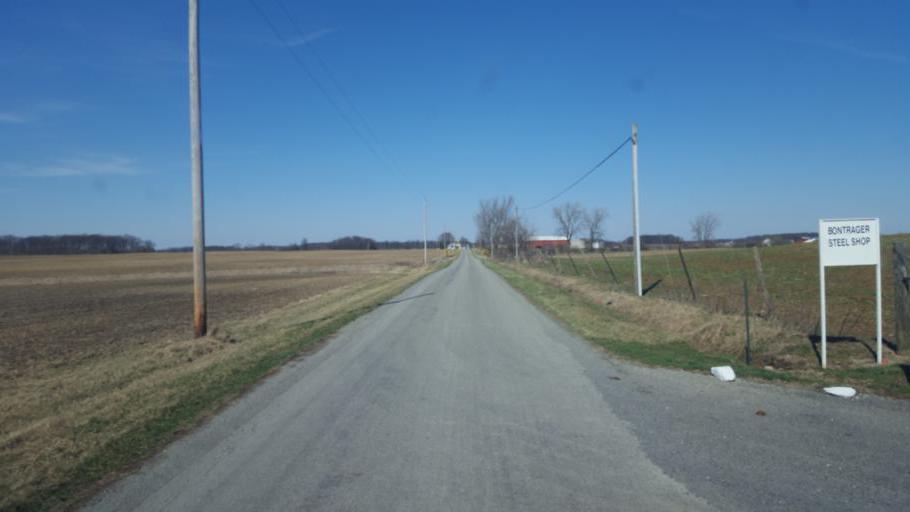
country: US
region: Ohio
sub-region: Hardin County
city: Kenton
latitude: 40.5355
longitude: -83.4560
